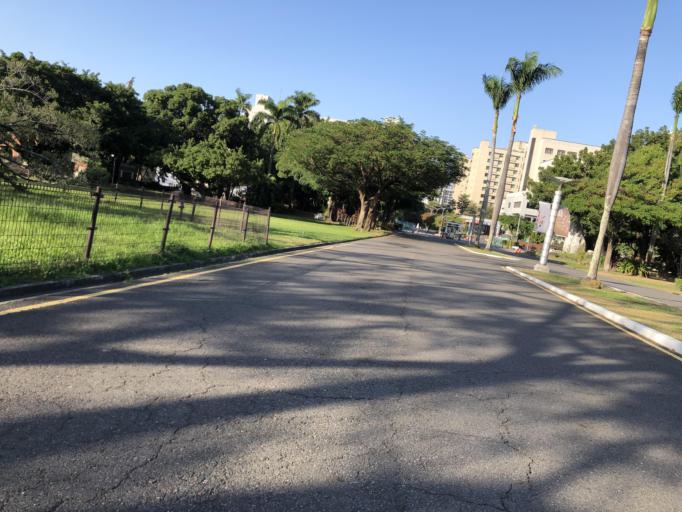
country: TW
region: Taiwan
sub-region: Tainan
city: Tainan
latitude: 23.0000
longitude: 120.2168
